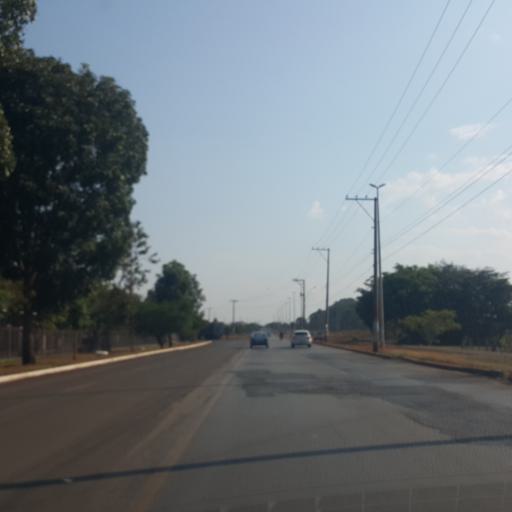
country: BR
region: Federal District
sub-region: Brasilia
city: Brasilia
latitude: -15.8712
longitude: -48.0415
